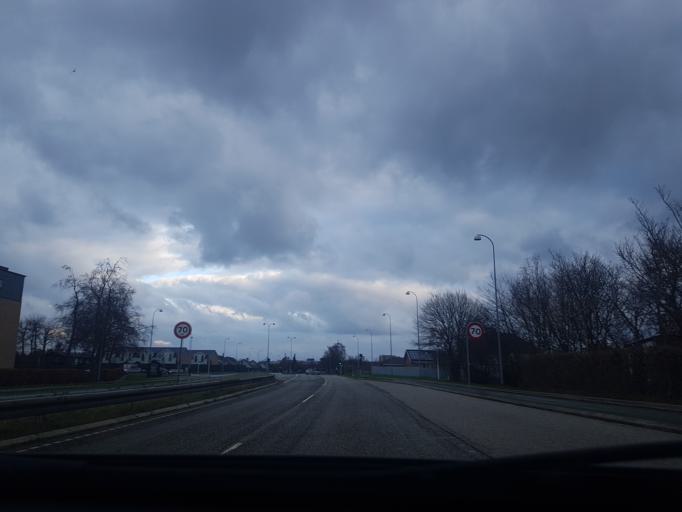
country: DK
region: Capital Region
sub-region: Vallensbaek Kommune
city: Vallensbaek
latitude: 55.6182
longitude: 12.3794
